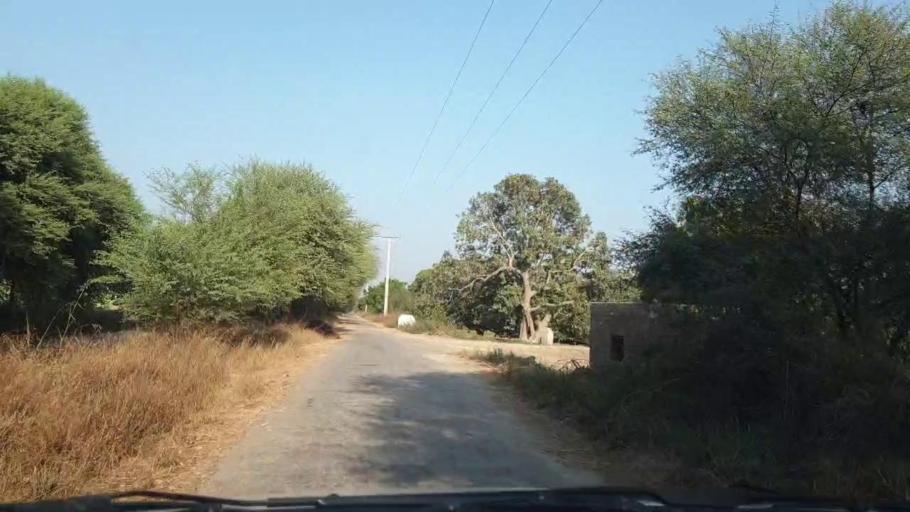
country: PK
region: Sindh
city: Tando Muhammad Khan
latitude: 25.2259
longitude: 68.6384
